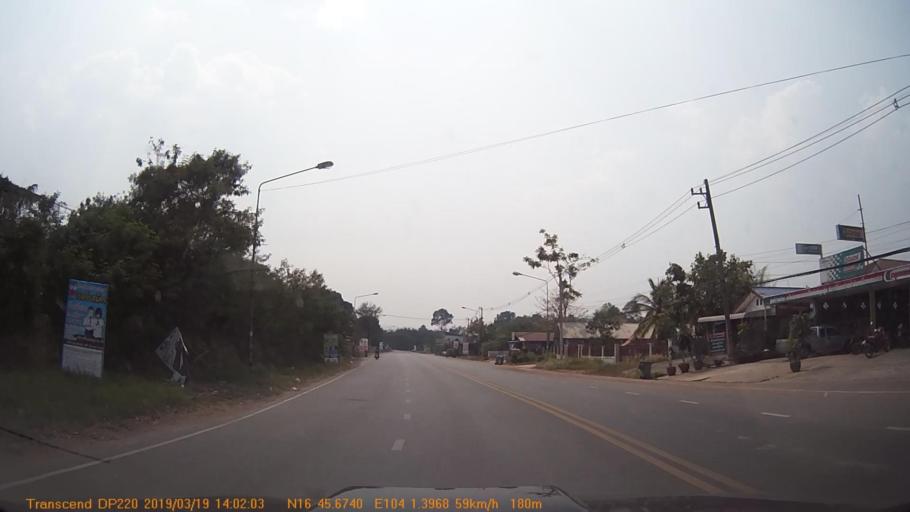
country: TH
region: Kalasin
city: Na Khu
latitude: 16.7612
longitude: 104.0229
